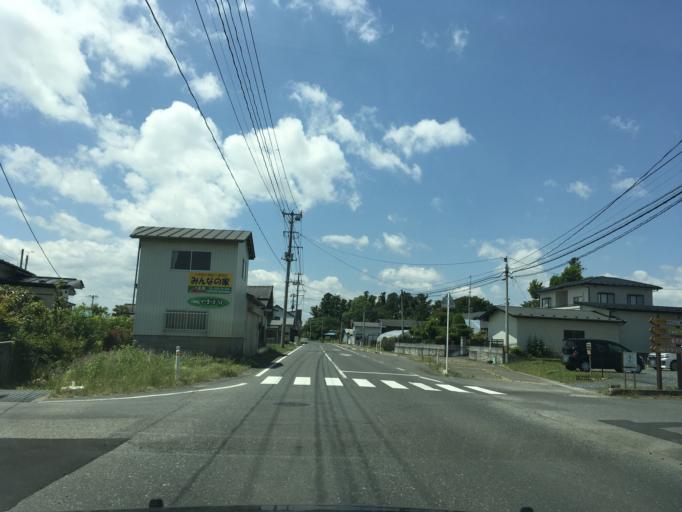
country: JP
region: Miyagi
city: Wakuya
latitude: 38.6759
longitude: 141.2516
